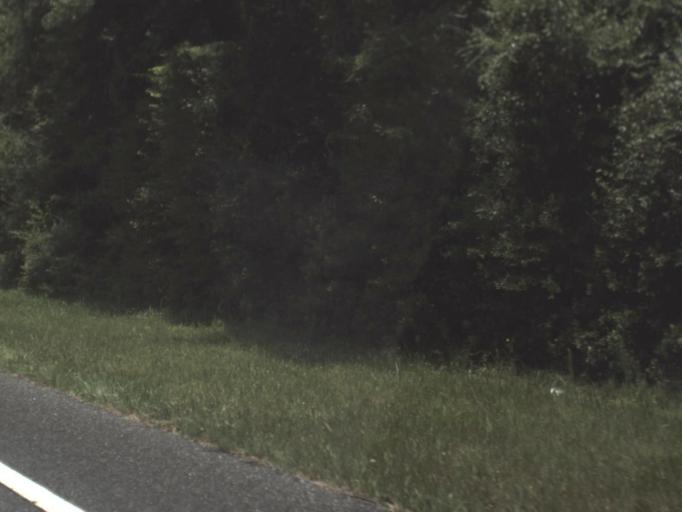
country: US
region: Florida
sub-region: Taylor County
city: Steinhatchee
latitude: 29.7424
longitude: -83.3191
